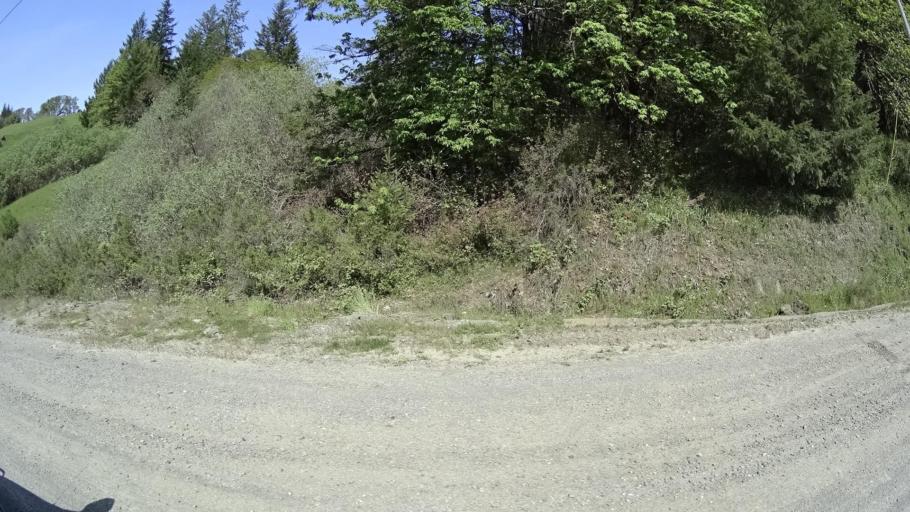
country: US
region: California
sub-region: Humboldt County
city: Redway
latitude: 40.4179
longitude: -123.7614
